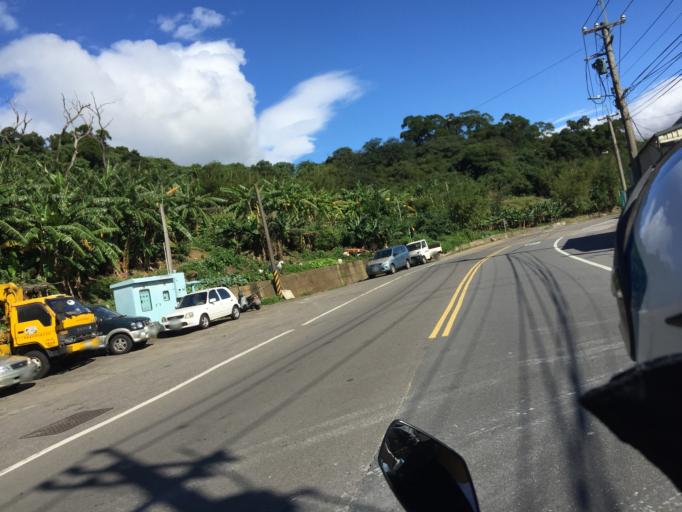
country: TW
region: Taipei
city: Taipei
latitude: 25.1823
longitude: 121.4598
